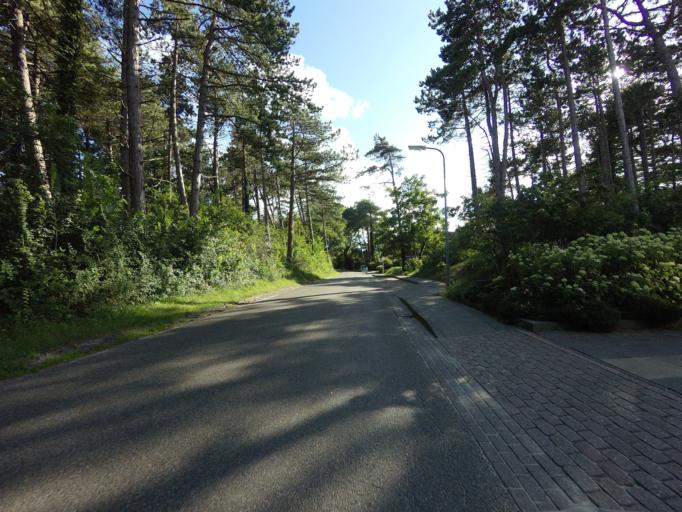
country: NL
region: Friesland
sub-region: Gemeente Terschelling
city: West-Terschelling
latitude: 53.3672
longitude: 5.2157
